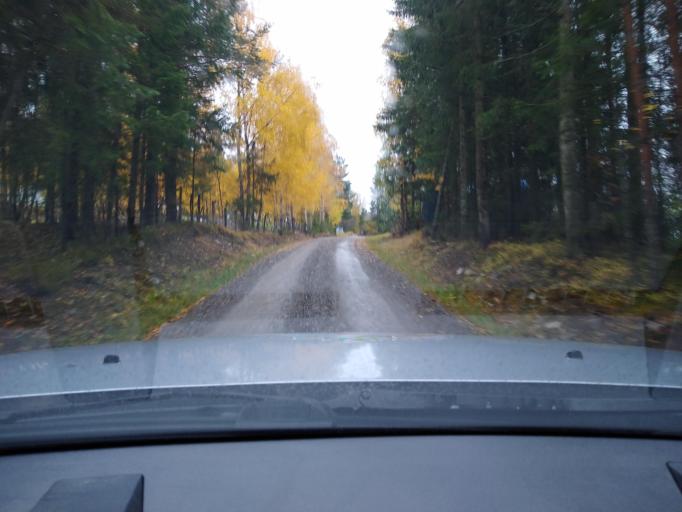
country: NO
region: Oppland
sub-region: Ringebu
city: Ringebu
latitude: 61.5527
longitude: 10.1530
